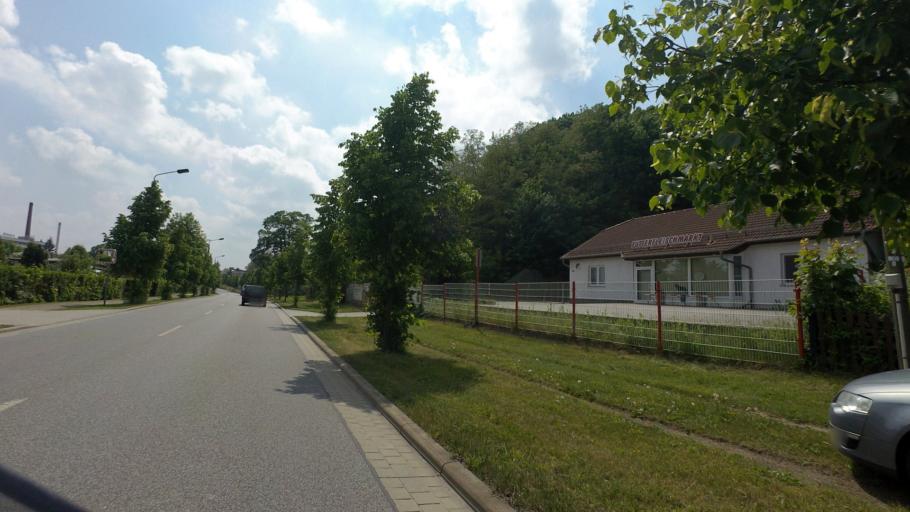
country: DE
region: Brandenburg
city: Spremberg
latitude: 51.5757
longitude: 14.3638
